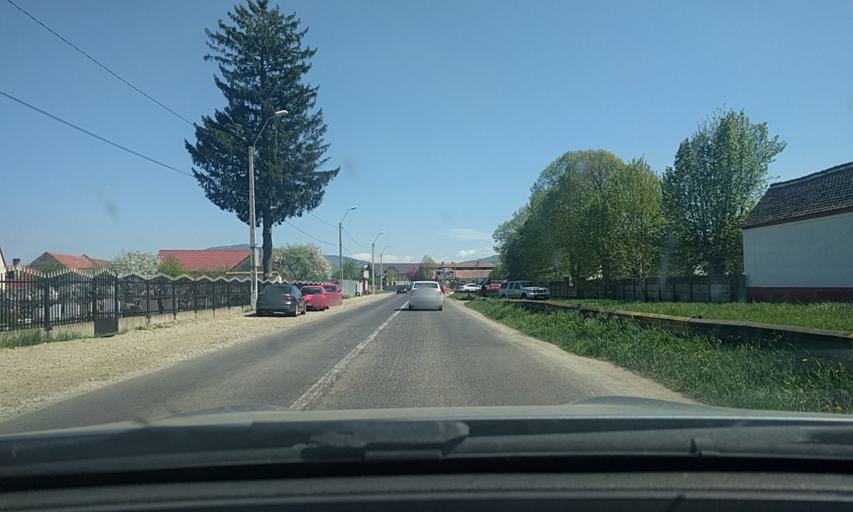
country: RO
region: Brasov
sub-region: Comuna Prejmer
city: Prejmer
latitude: 45.7143
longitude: 25.7789
